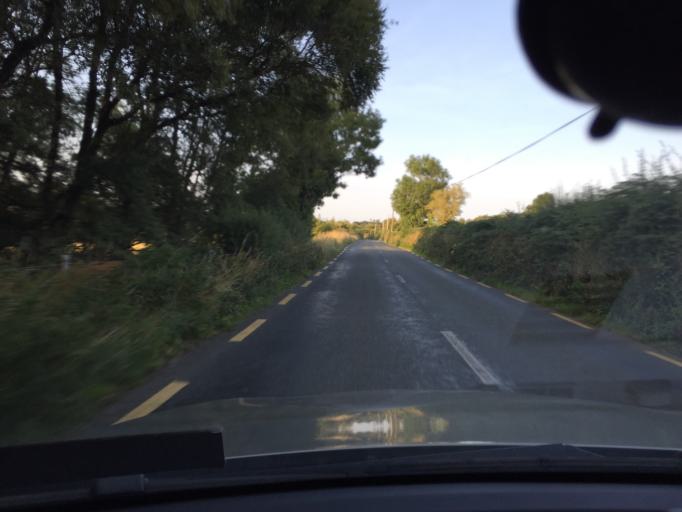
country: IE
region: Leinster
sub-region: Wicklow
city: Rathdrum
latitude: 53.0490
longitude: -6.2406
